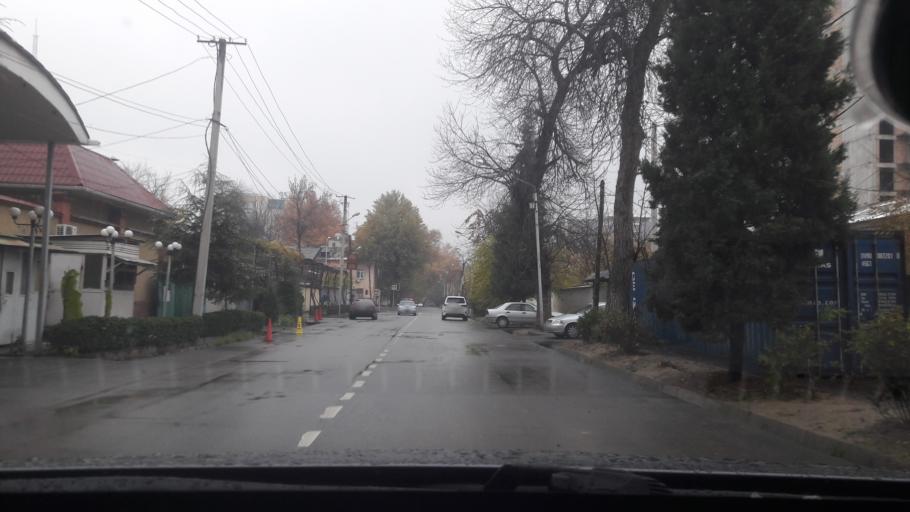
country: TJ
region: Dushanbe
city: Dushanbe
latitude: 38.5742
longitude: 68.7960
